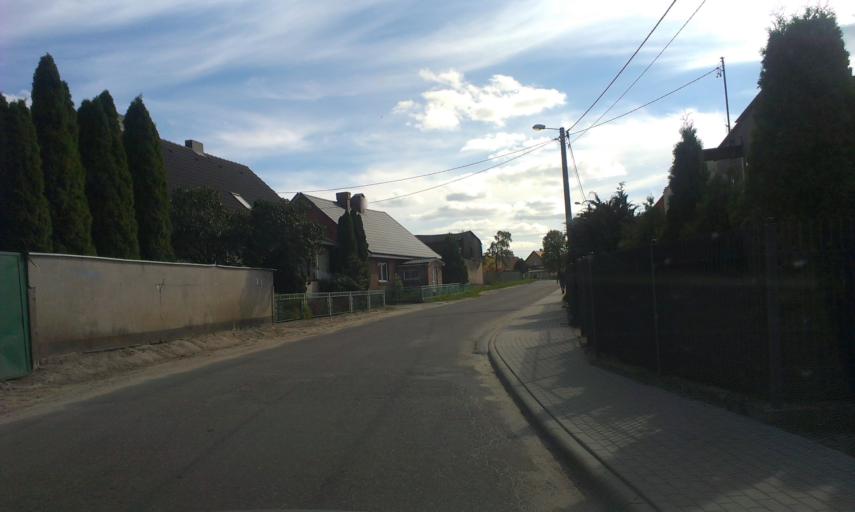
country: PL
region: Greater Poland Voivodeship
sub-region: Powiat zlotowski
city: Zlotow
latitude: 53.3069
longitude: 17.1282
